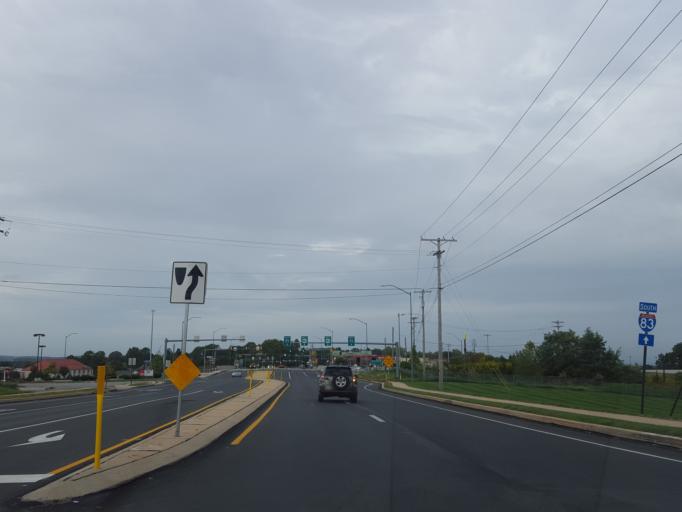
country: US
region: Pennsylvania
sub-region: York County
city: Spry
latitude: 39.9107
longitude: -76.7007
